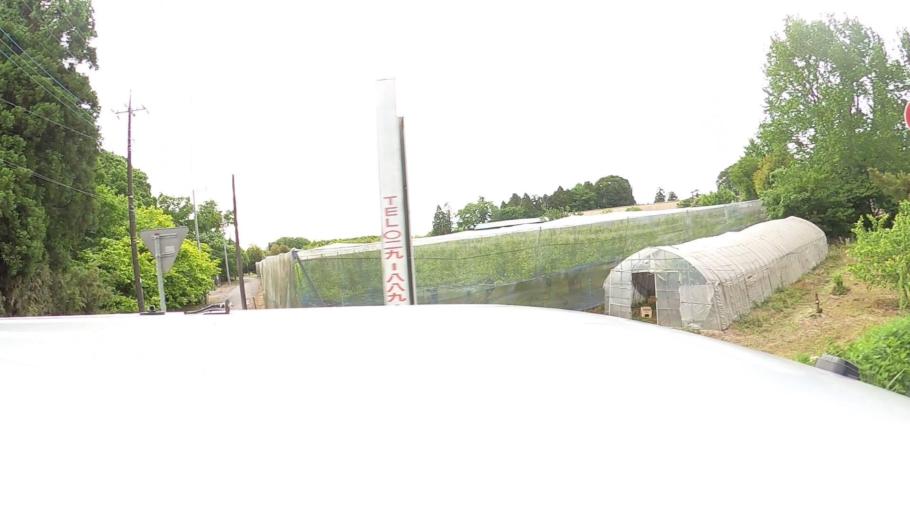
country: JP
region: Ibaraki
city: Ami
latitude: 35.9833
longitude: 140.2446
